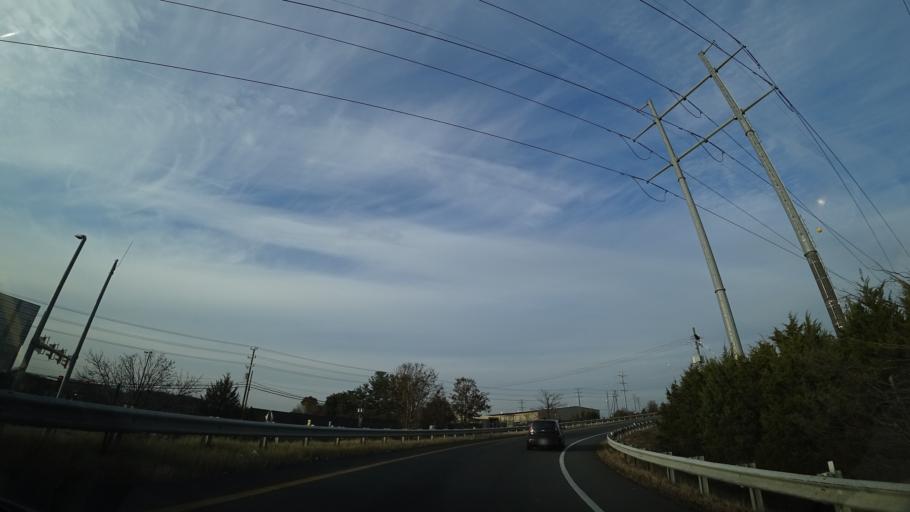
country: US
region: Virginia
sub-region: Fairfax County
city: Newington
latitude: 38.7402
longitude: -77.1919
